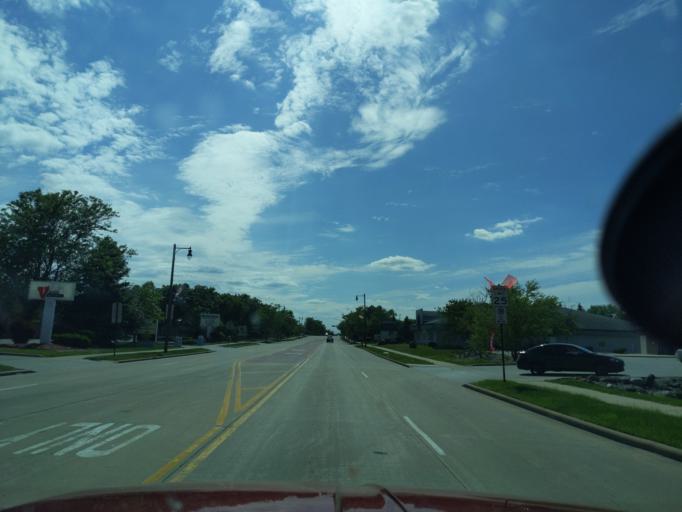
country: US
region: Wisconsin
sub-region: Dane County
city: Sun Prairie
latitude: 43.1801
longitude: -89.2332
